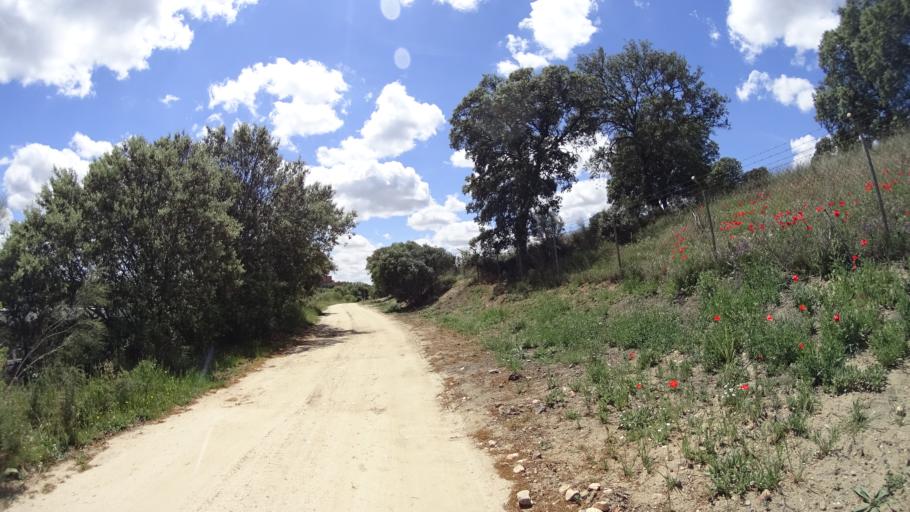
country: ES
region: Madrid
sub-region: Provincia de Madrid
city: Villanueva del Pardillo
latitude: 40.4435
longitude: -3.9539
